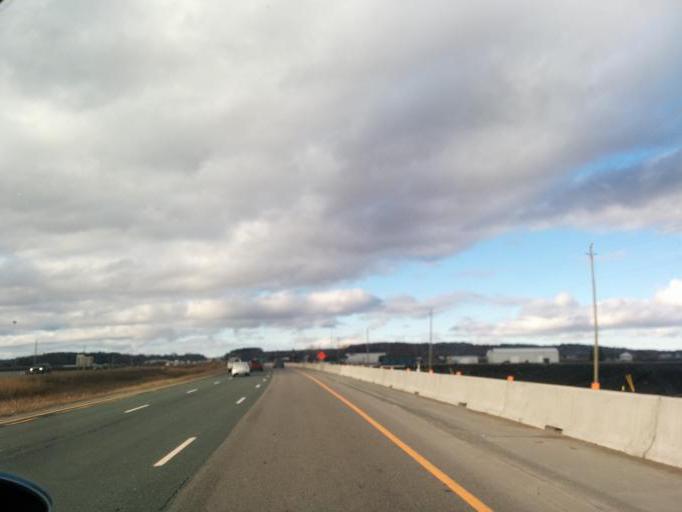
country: CA
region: Ontario
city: Bradford West Gwillimbury
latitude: 44.0382
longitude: -79.5969
